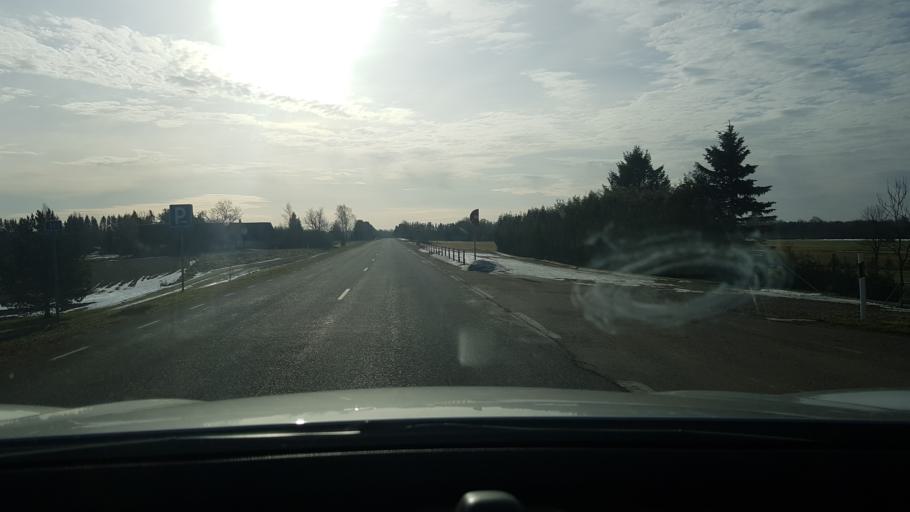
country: EE
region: Saare
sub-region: Kuressaare linn
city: Kuressaare
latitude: 58.5214
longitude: 22.7018
